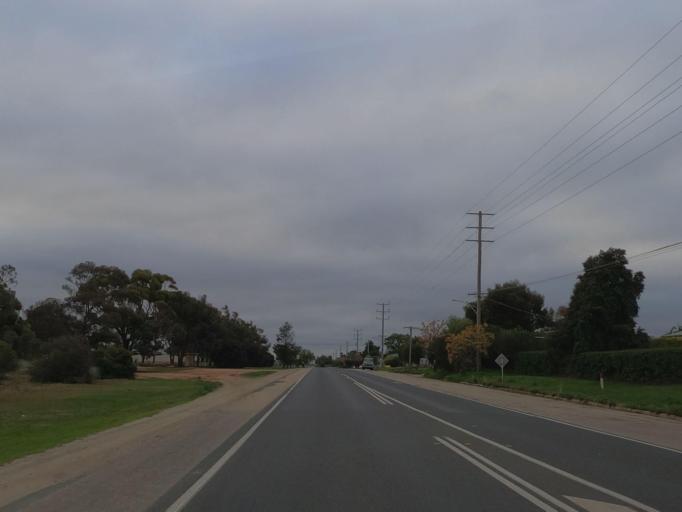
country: AU
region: Victoria
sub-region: Swan Hill
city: Swan Hill
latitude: -35.4608
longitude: 143.6335
